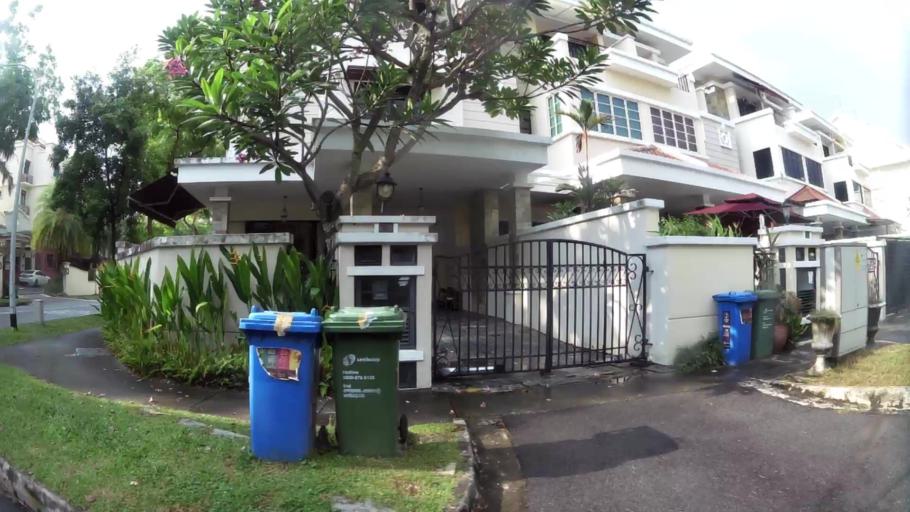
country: SG
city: Singapore
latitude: 1.3208
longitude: 103.9567
